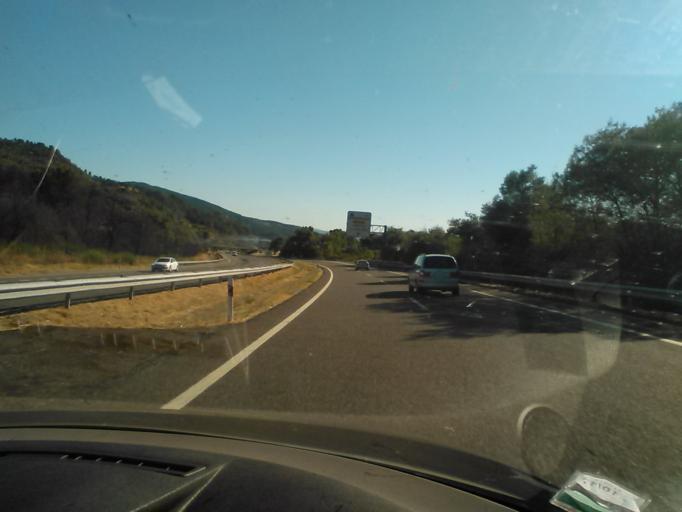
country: ES
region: Galicia
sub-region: Provincia de Ourense
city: Verin
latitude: 41.9428
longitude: -7.3946
